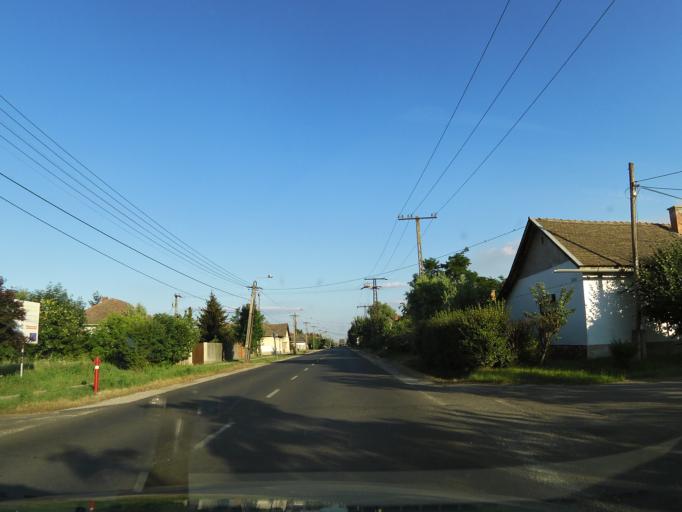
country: HU
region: Jasz-Nagykun-Szolnok
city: Kunszentmarton
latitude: 46.8467
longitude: 20.2813
